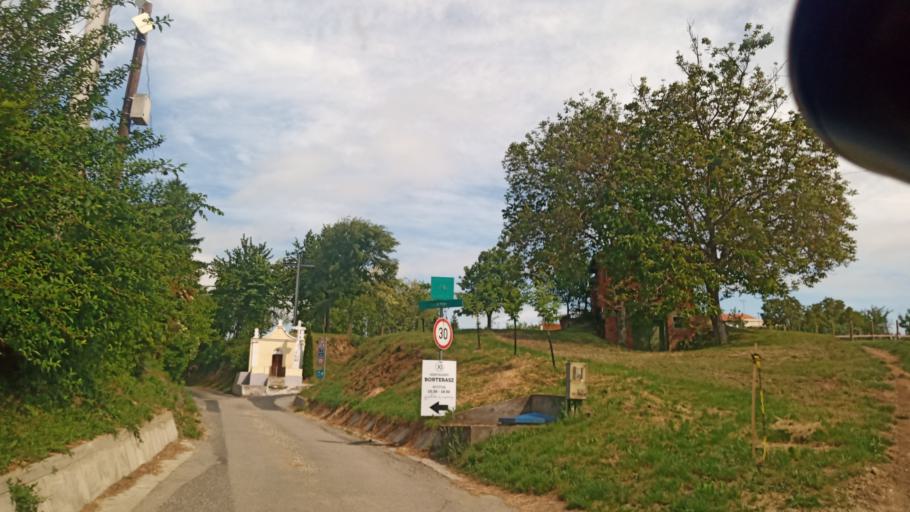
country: HU
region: Zala
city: Sarmellek
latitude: 46.6379
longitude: 17.1008
